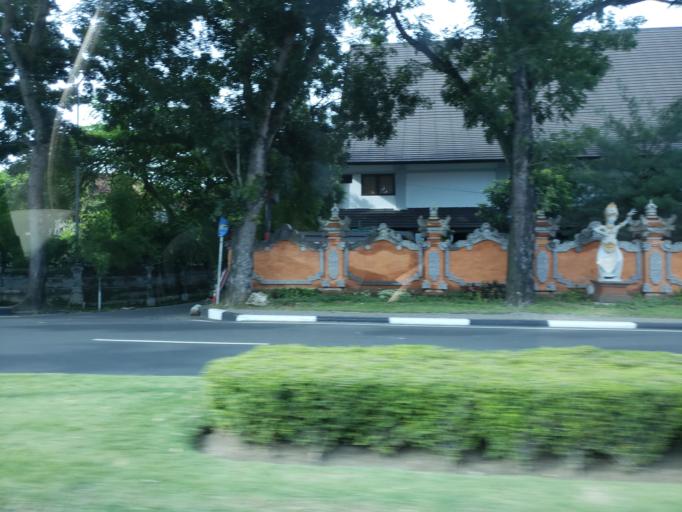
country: ID
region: Bali
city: Kelanabian
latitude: -8.7447
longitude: 115.1779
